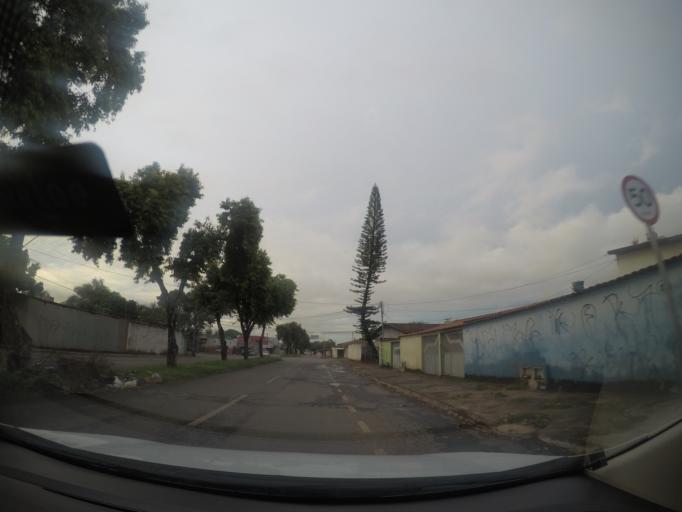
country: BR
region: Goias
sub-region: Goiania
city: Goiania
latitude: -16.6959
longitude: -49.3115
